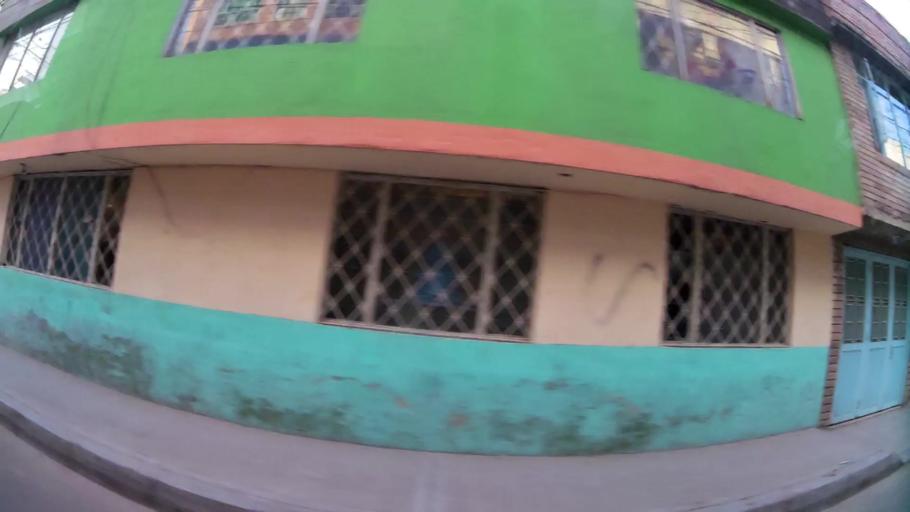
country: CO
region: Cundinamarca
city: Soacha
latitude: 4.6280
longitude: -74.1679
